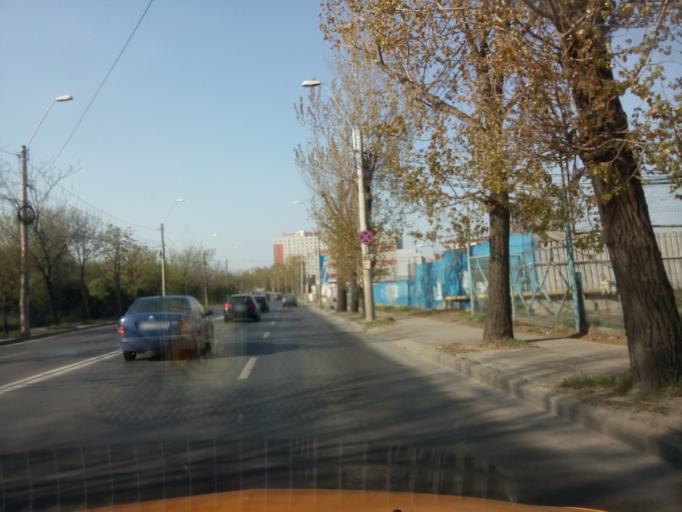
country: RO
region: Ilfov
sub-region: Comuna Popesti-Leordeni
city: Popesti-Leordeni
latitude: 44.3937
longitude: 26.1429
